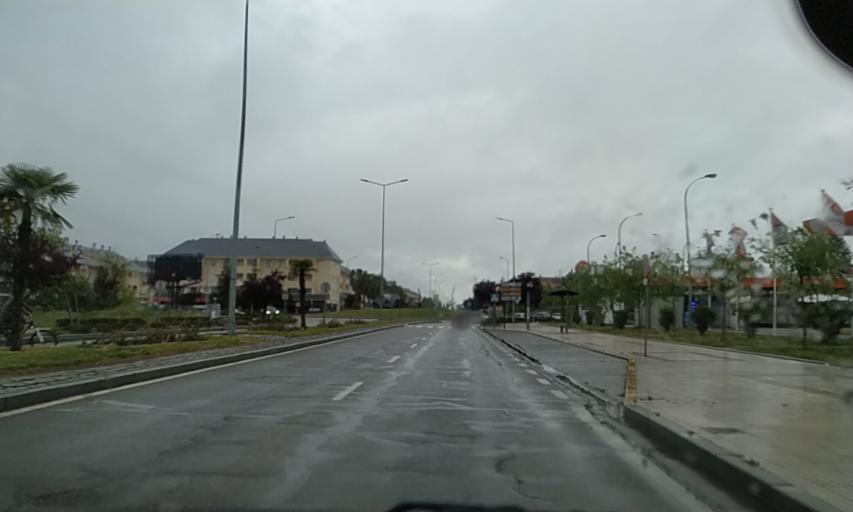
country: ES
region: Extremadura
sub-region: Provincia de Badajoz
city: Badajoz
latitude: 38.8836
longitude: -6.9898
